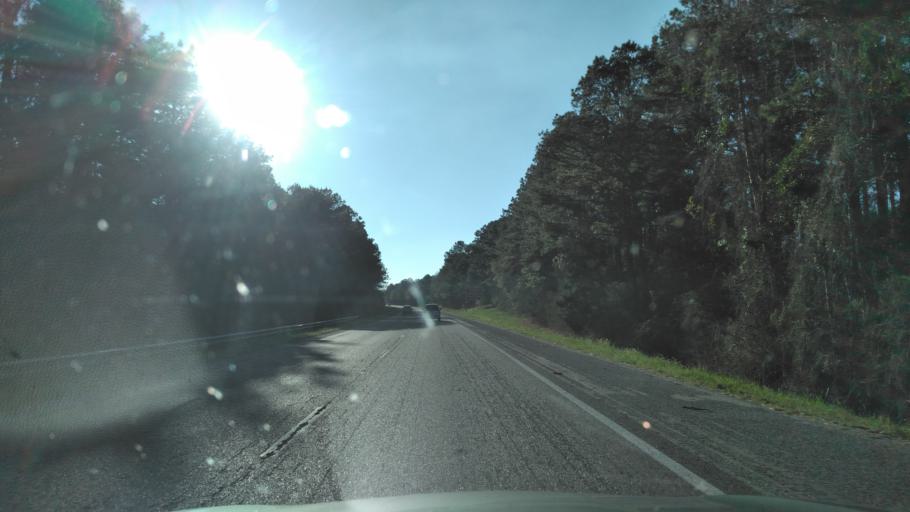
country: US
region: Alabama
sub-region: Baldwin County
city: Bay Minette
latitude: 30.9525
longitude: -87.8408
